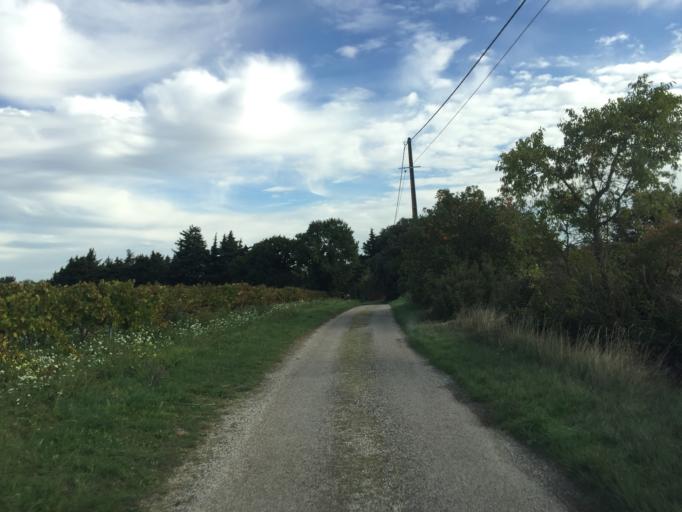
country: FR
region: Provence-Alpes-Cote d'Azur
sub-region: Departement du Vaucluse
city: Orange
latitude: 44.1123
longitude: 4.8088
